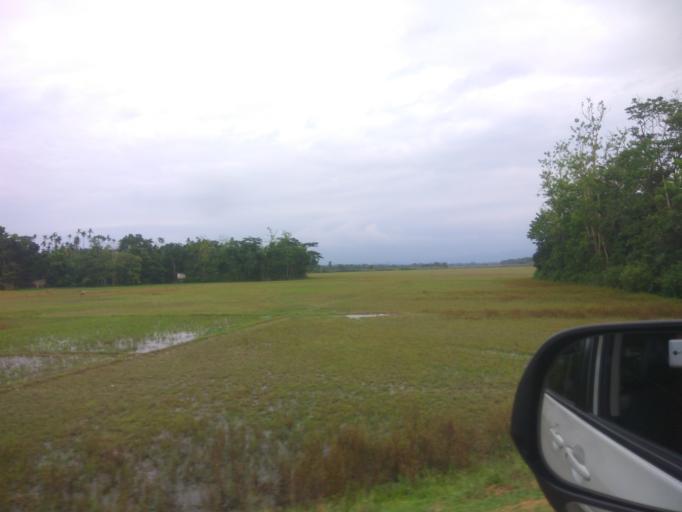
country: IN
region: Assam
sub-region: Karimganj
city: Karimganj
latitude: 24.9492
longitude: 92.2400
